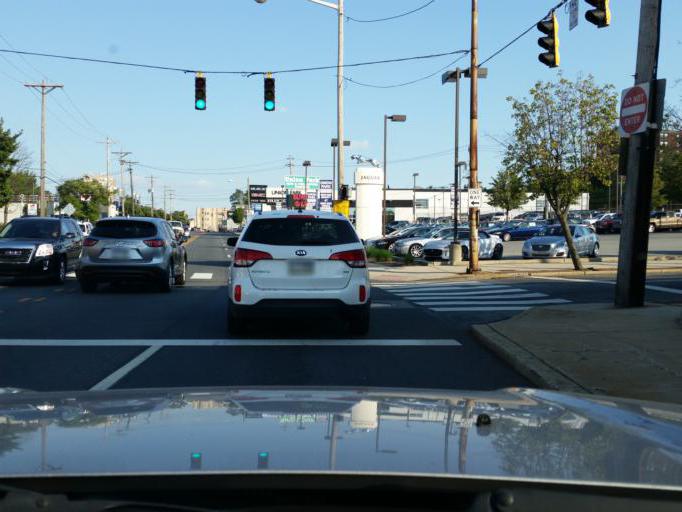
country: US
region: Delaware
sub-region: New Castle County
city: Wilmington
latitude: 39.7557
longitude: -75.5673
